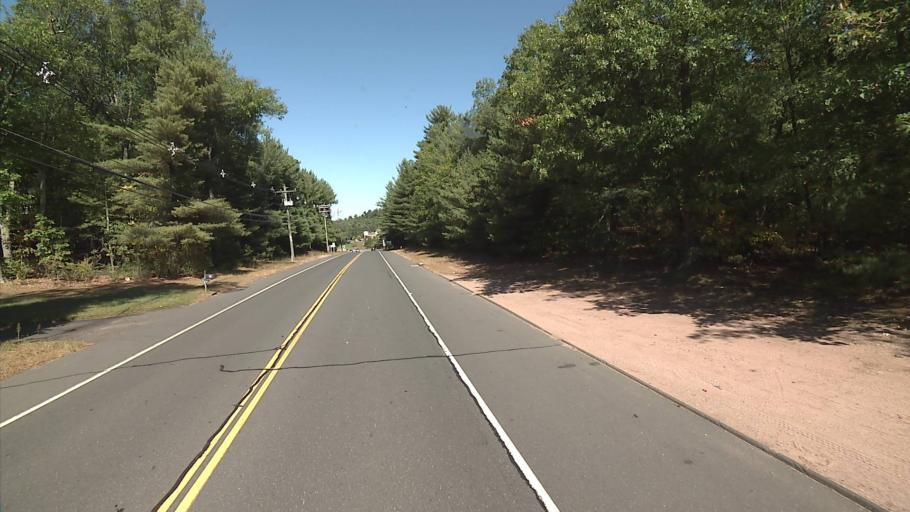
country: US
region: Connecticut
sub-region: Hartford County
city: Manchester
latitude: 41.7102
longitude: -72.5275
